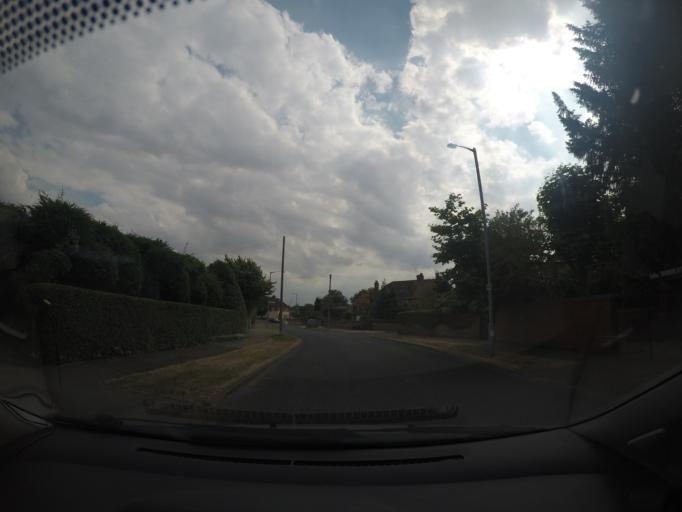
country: GB
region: England
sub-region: City of York
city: York
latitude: 53.9524
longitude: -1.1185
